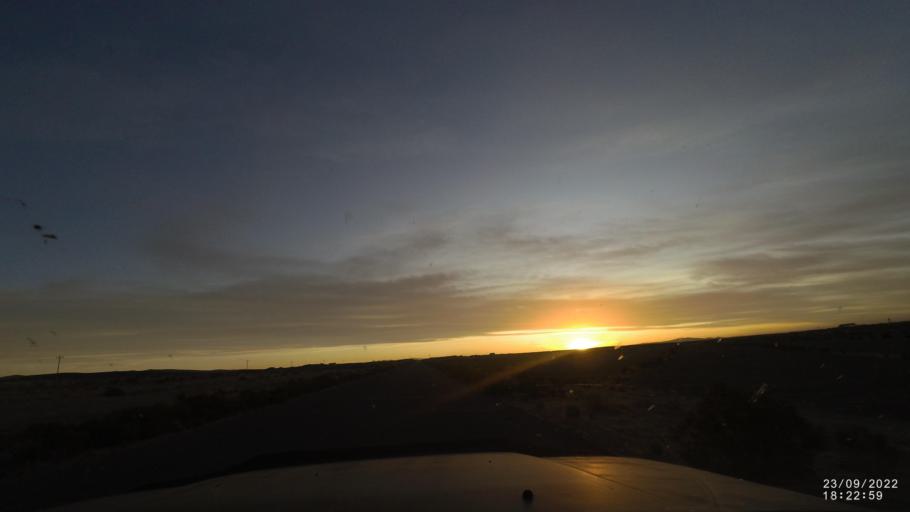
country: BO
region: Oruro
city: Challapata
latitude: -19.2921
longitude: -67.0954
